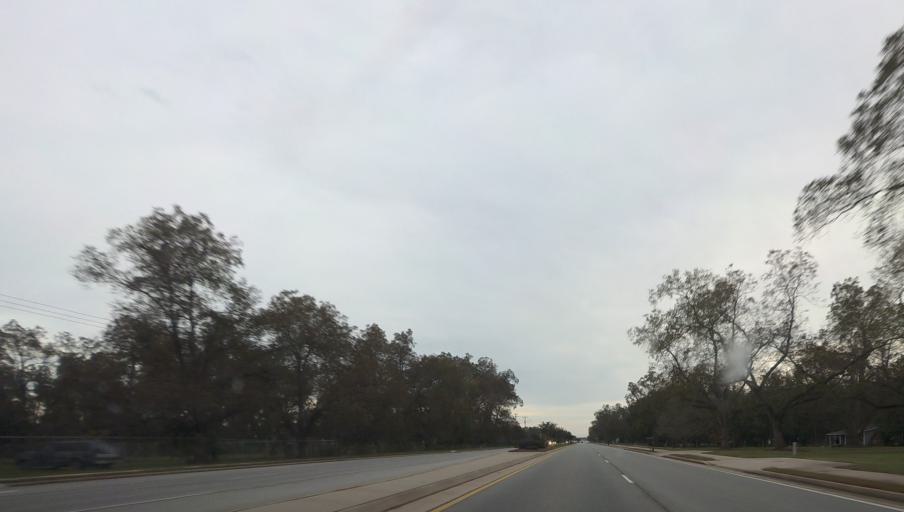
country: US
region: Georgia
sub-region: Houston County
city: Perry
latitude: 32.5242
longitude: -83.6624
